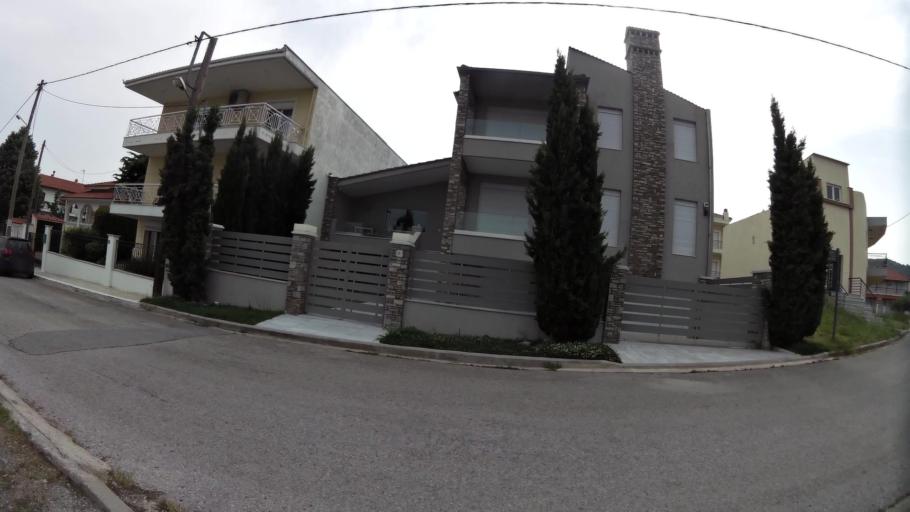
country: GR
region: Central Macedonia
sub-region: Nomos Thessalonikis
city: Oraiokastro
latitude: 40.7359
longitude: 22.9222
